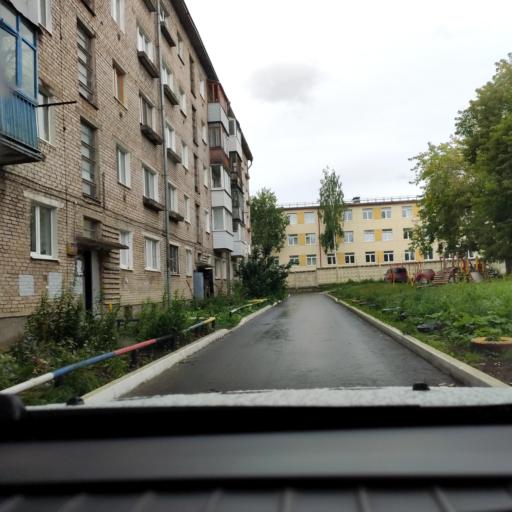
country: RU
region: Perm
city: Perm
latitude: 58.1187
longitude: 56.3100
